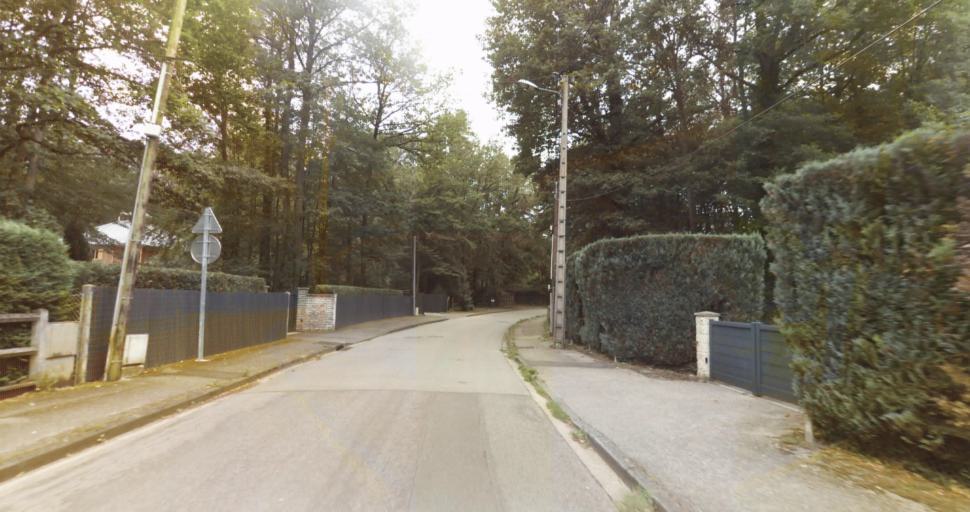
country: FR
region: Haute-Normandie
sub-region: Departement de l'Eure
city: La Couture-Boussey
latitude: 48.8950
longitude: 1.3964
